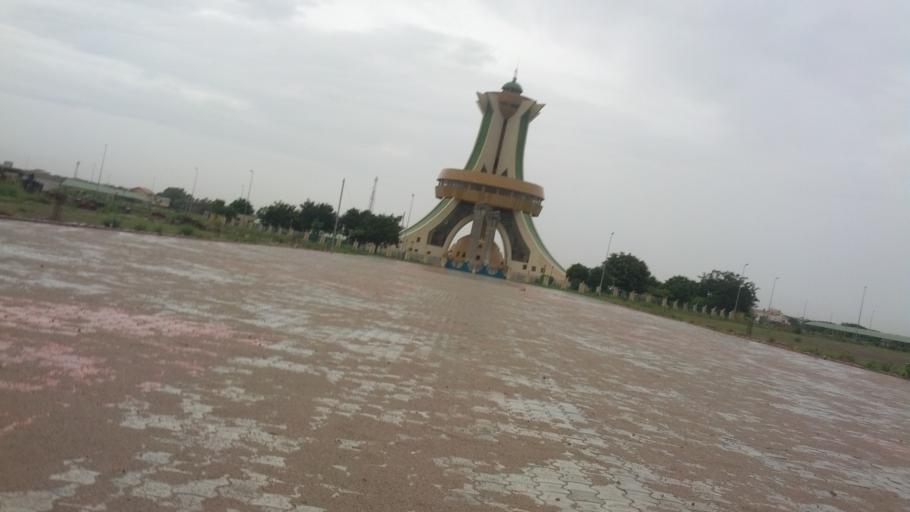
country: BF
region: Centre
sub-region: Kadiogo Province
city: Ouagadougou
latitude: 12.3100
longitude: -1.5027
